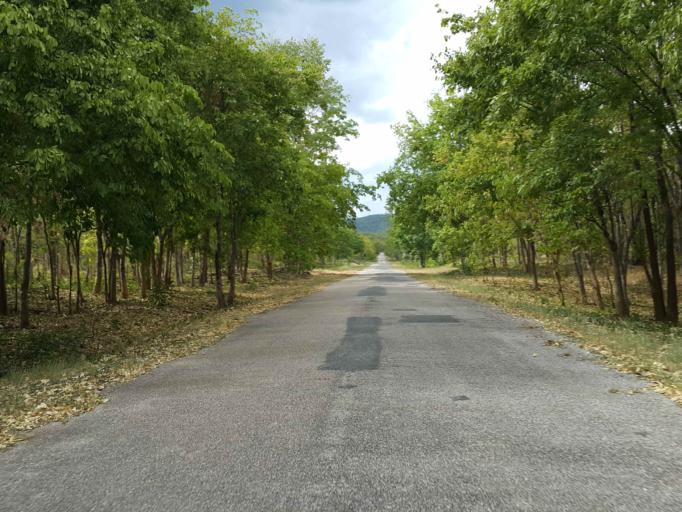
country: TH
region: Sukhothai
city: Thung Saliam
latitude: 17.3397
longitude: 99.4239
